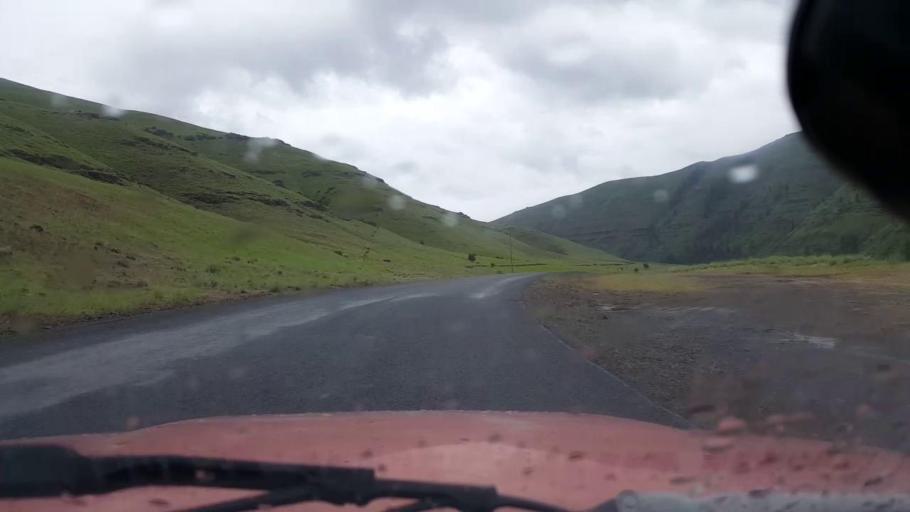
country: US
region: Washington
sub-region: Asotin County
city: Asotin
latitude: 46.0410
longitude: -117.2921
